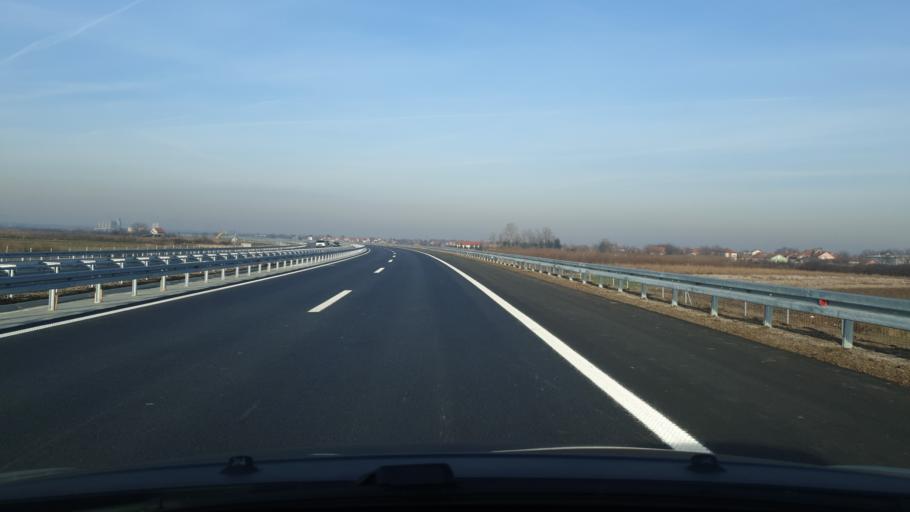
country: RS
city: Boljevci
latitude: 44.7475
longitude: 20.2500
